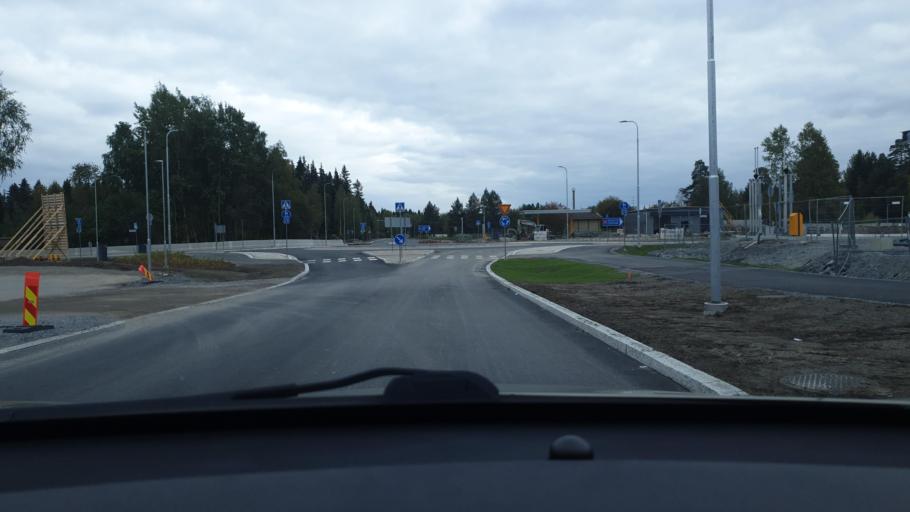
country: FI
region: Ostrobothnia
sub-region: Vaasa
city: Teeriniemi
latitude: 63.0724
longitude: 21.7009
